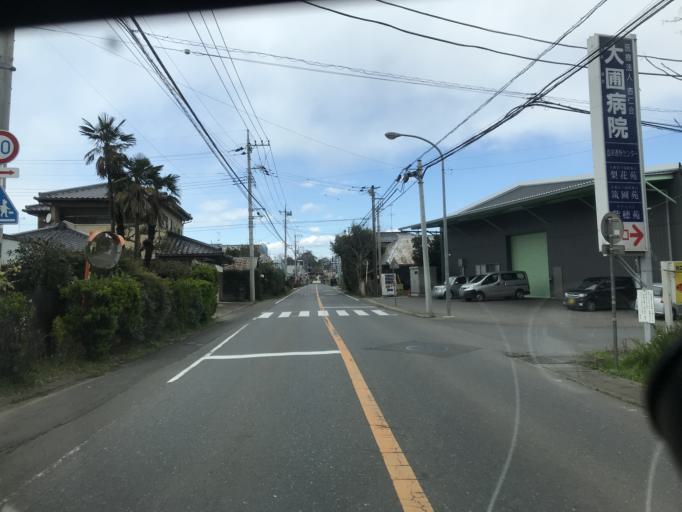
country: JP
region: Ibaraki
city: Shimodate
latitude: 36.2432
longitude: 139.9775
